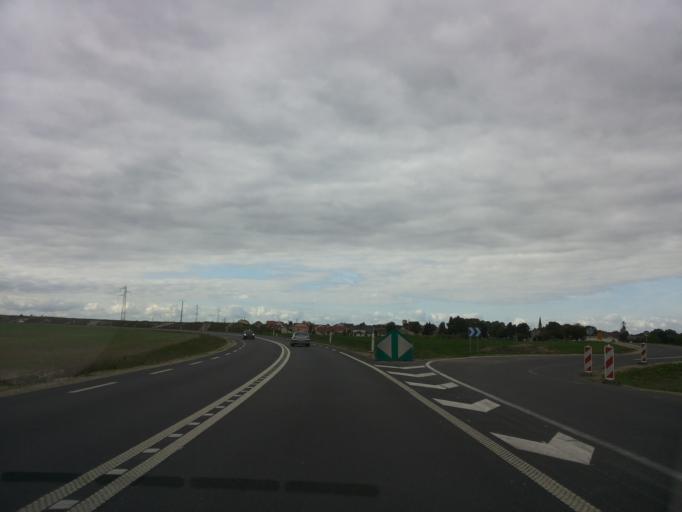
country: FR
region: Champagne-Ardenne
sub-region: Departement de la Marne
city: Verzy
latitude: 49.1675
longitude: 4.1929
